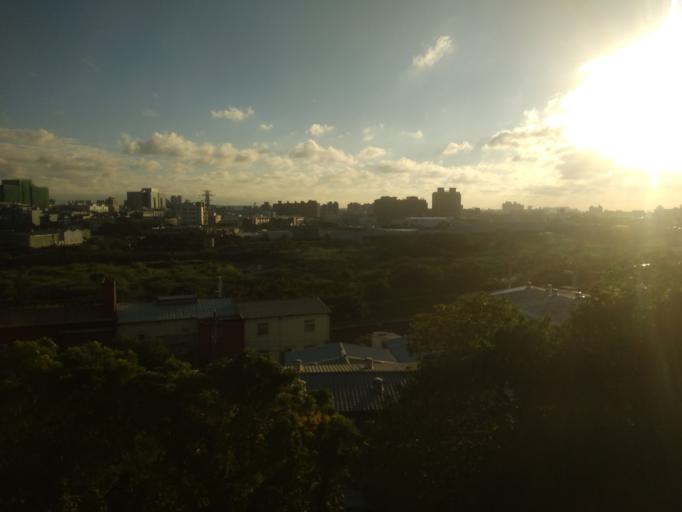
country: TW
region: Taiwan
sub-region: Hsinchu
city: Zhubei
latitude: 24.8543
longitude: 121.0092
